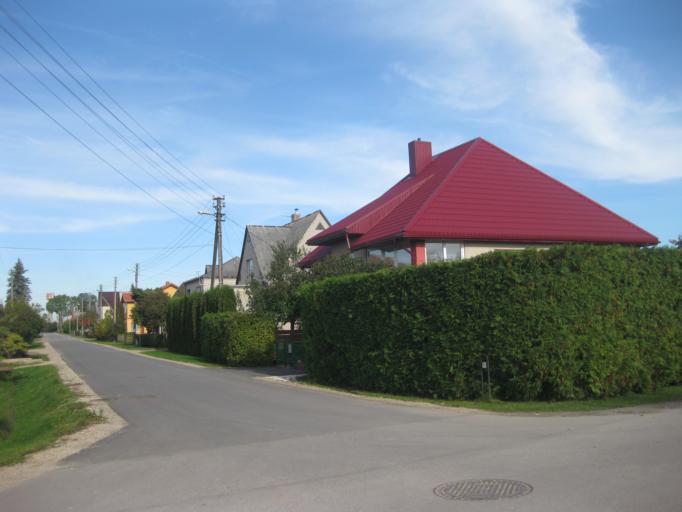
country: LT
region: Kauno apskritis
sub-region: Kauno rajonas
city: Garliava
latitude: 54.8231
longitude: 23.8774
